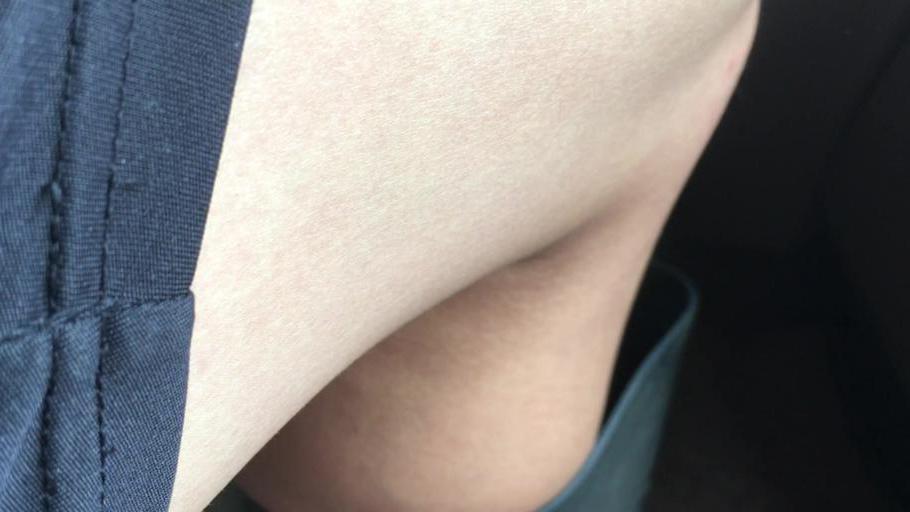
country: US
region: Maryland
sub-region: Worcester County
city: Pocomoke City
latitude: 38.0658
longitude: -75.5142
